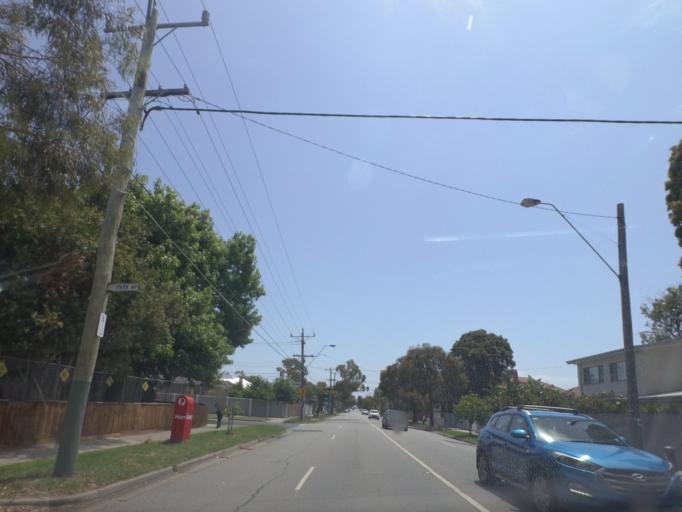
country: AU
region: Victoria
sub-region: Bayside
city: Black Rock
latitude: -37.9575
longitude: 145.0198
